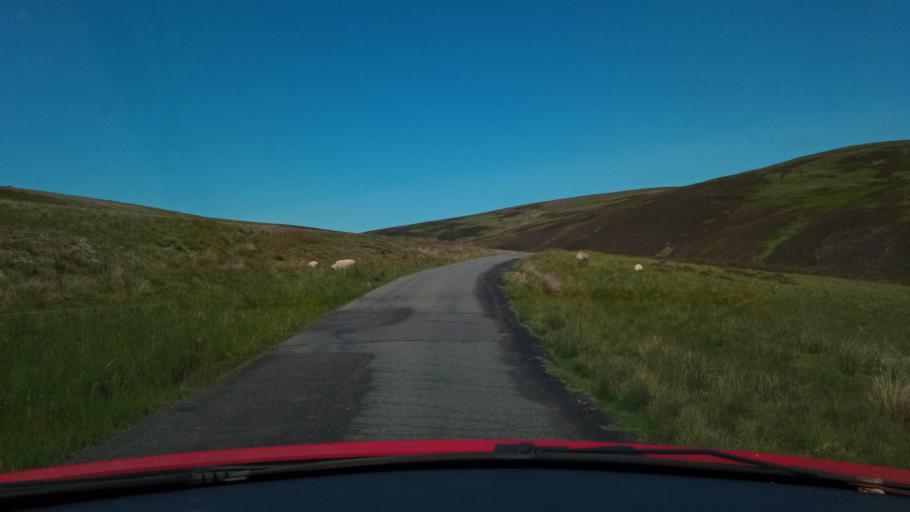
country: GB
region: Scotland
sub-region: East Lothian
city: East Linton
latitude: 55.8448
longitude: -2.5859
